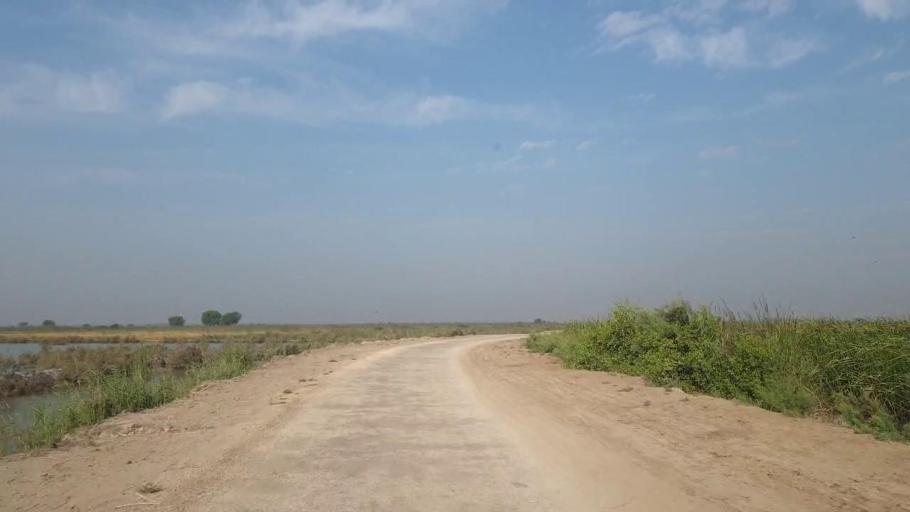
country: PK
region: Sindh
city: Tando Bago
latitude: 24.8451
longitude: 68.9752
